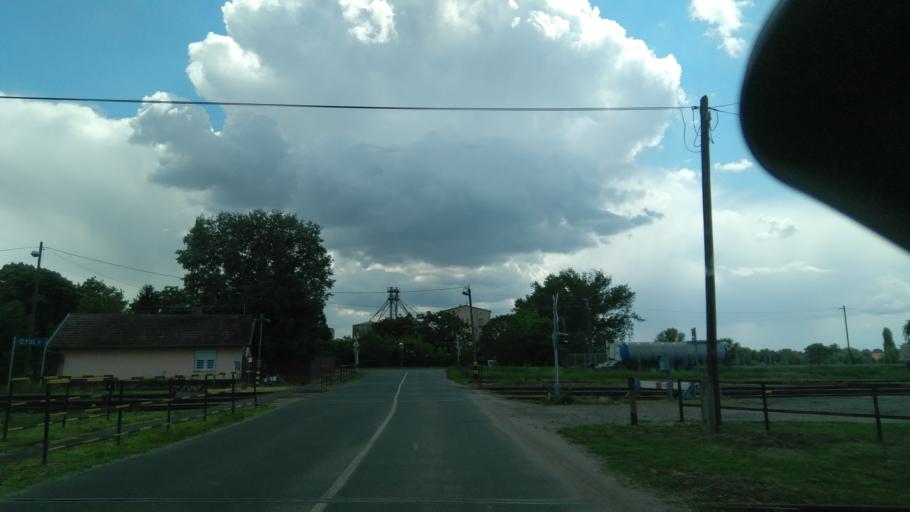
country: HU
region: Bekes
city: Gyula
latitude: 46.6569
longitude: 21.2695
